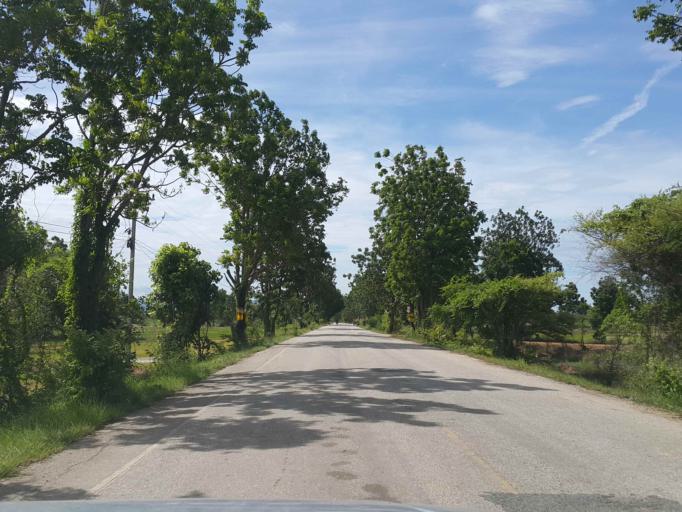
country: TH
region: Sukhothai
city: Ban Dan Lan Hoi
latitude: 17.1403
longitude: 99.5238
